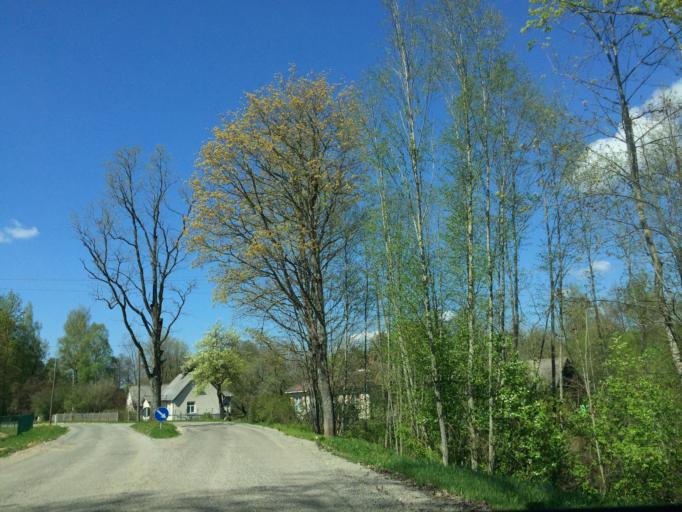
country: LV
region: Baldone
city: Baldone
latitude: 56.7407
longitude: 24.3739
